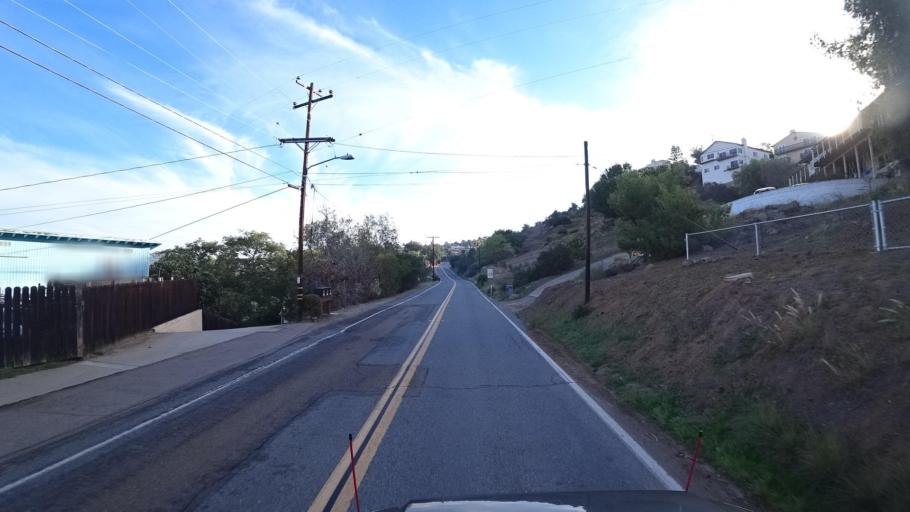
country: US
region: California
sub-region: San Diego County
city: Spring Valley
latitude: 32.7268
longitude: -117.0002
